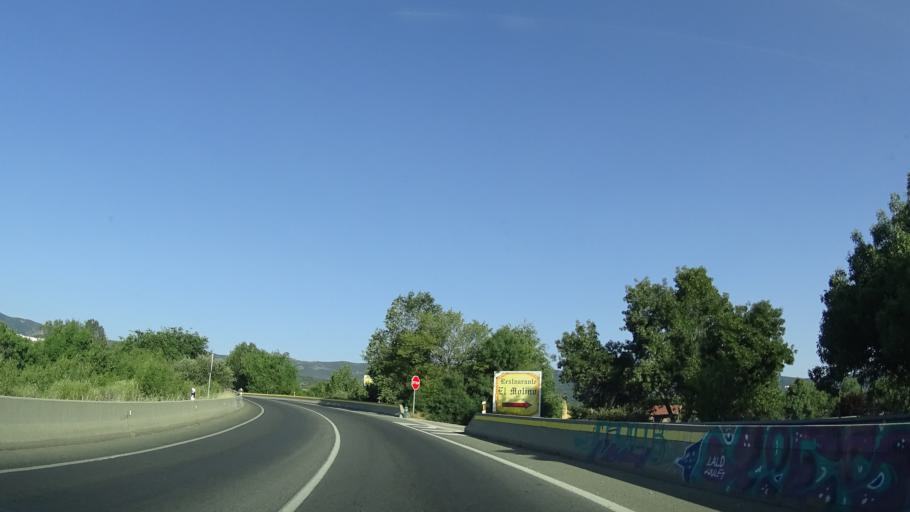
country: ES
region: Madrid
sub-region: Provincia de Madrid
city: Guadarrama
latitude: 40.6652
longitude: -4.0774
